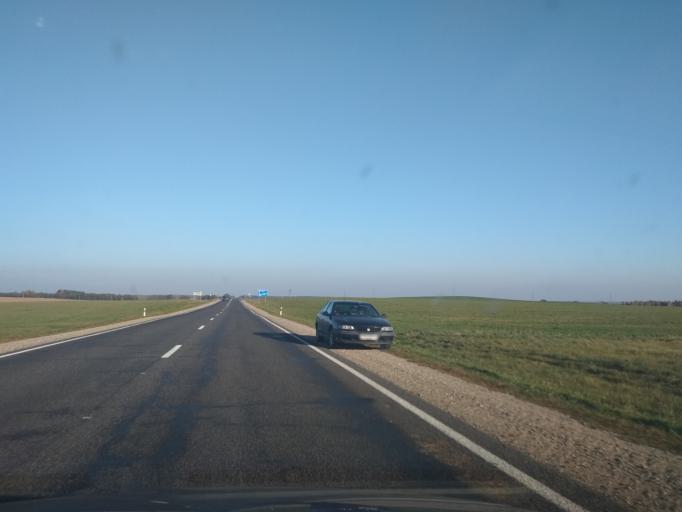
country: BY
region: Grodnenskaya
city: Svislach
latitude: 53.1328
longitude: 24.2087
